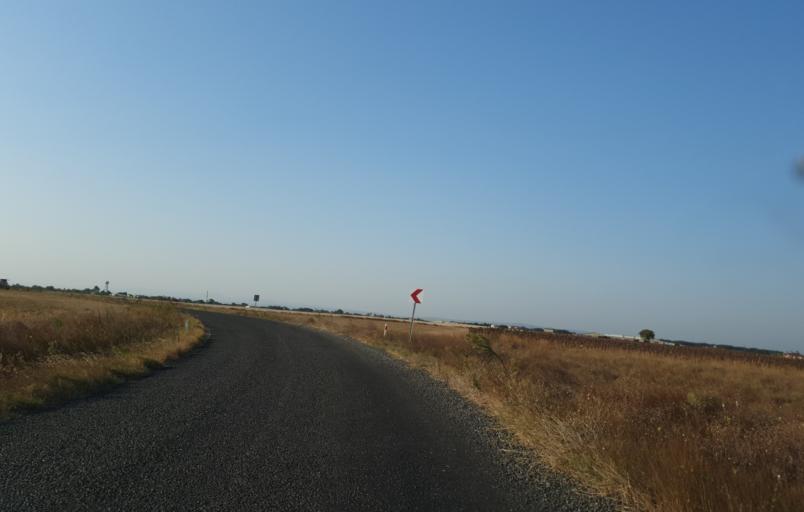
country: TR
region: Tekirdag
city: Beyazkoy
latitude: 41.4223
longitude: 27.7620
